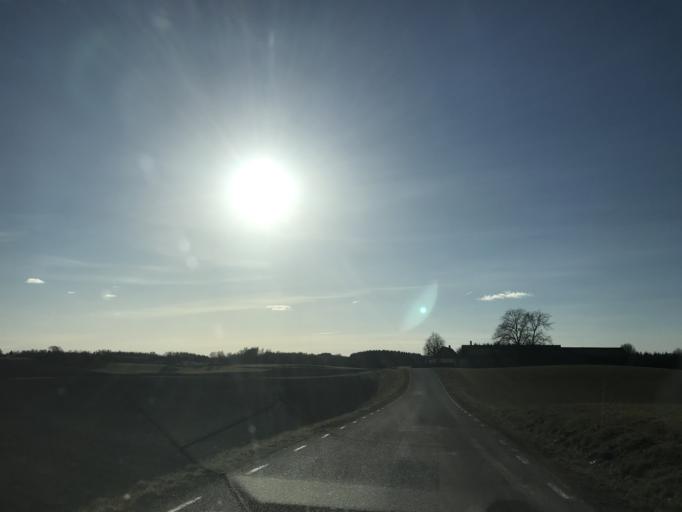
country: SE
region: Skane
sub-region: Ystads Kommun
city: Ystad
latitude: 55.5338
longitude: 13.7824
